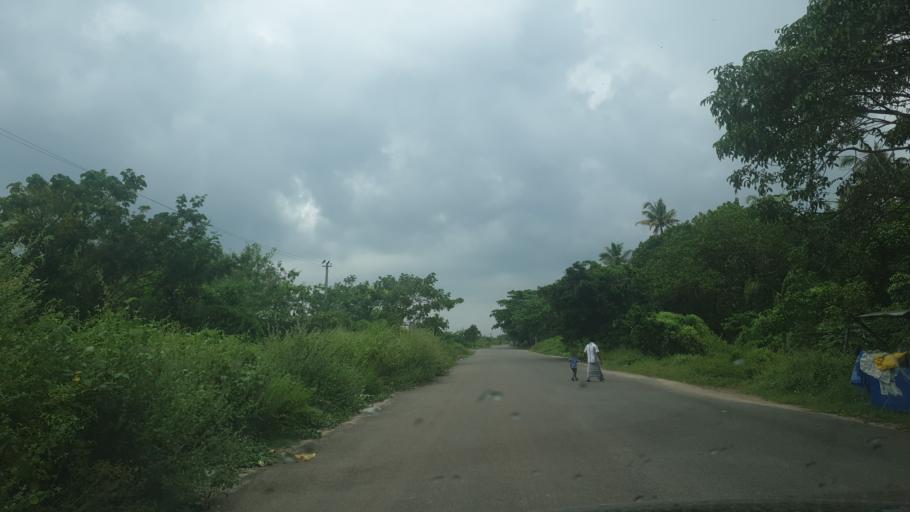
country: IN
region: Kerala
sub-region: Ernakulam
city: Cochin
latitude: 9.9995
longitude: 76.2206
